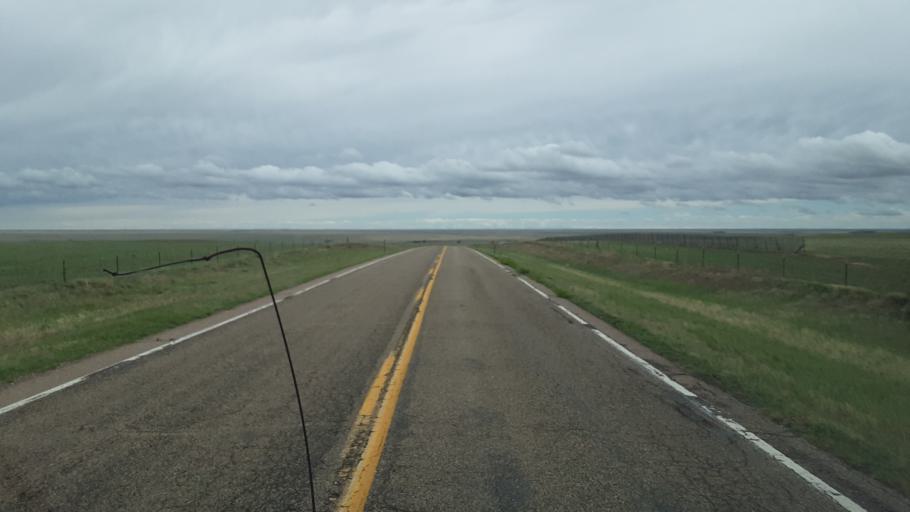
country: US
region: Colorado
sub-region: Lincoln County
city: Limon
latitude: 38.8451
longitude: -103.8026
